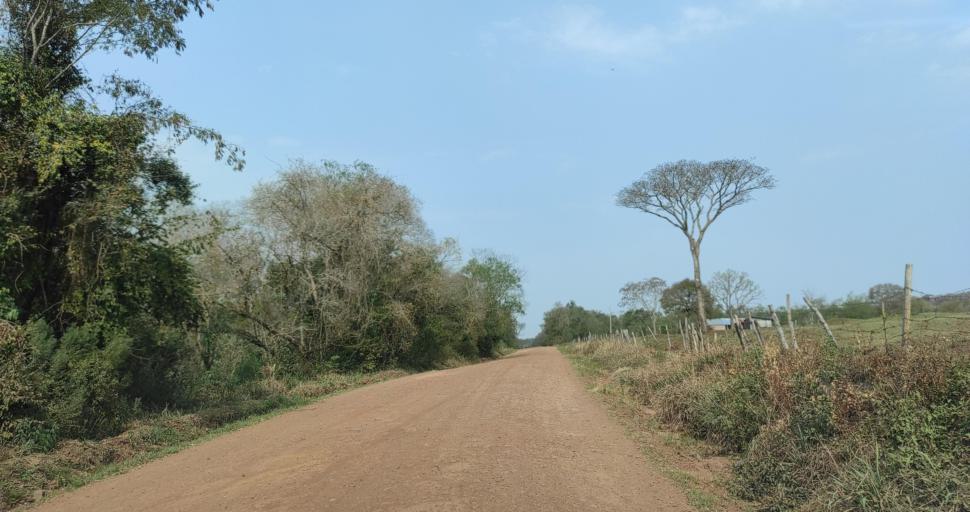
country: AR
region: Misiones
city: Cerro Cora
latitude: -27.5206
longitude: -55.6004
